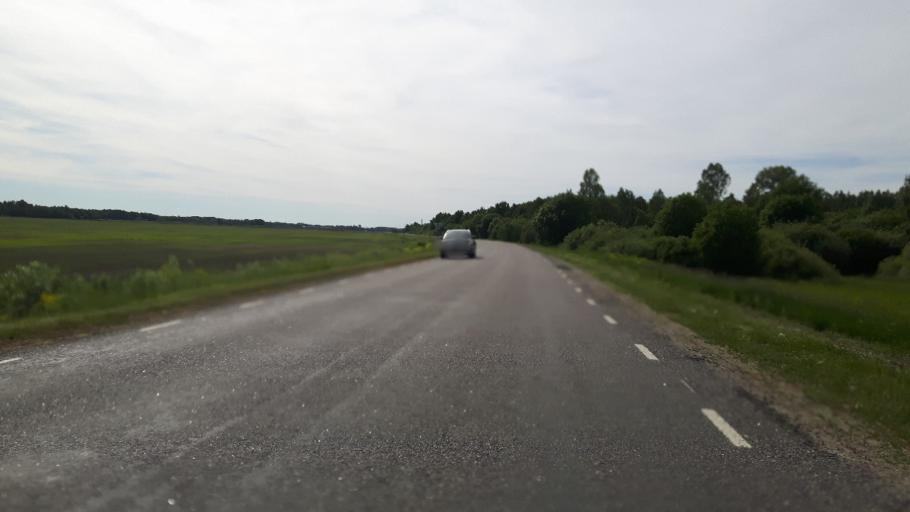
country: EE
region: Harju
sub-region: Raasiku vald
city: Arukula
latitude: 59.4261
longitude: 25.0747
